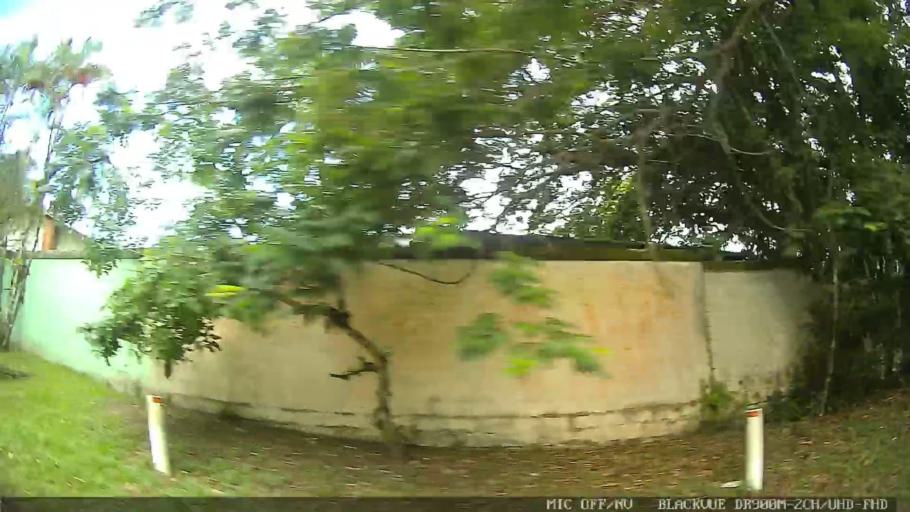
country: BR
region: Sao Paulo
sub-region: Iguape
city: Iguape
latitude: -24.6943
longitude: -47.5323
